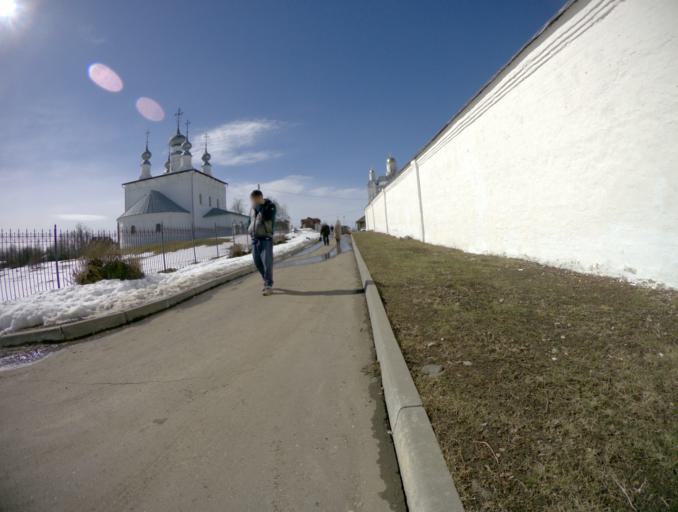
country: RU
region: Vladimir
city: Suzdal'
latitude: 56.4282
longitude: 40.4373
